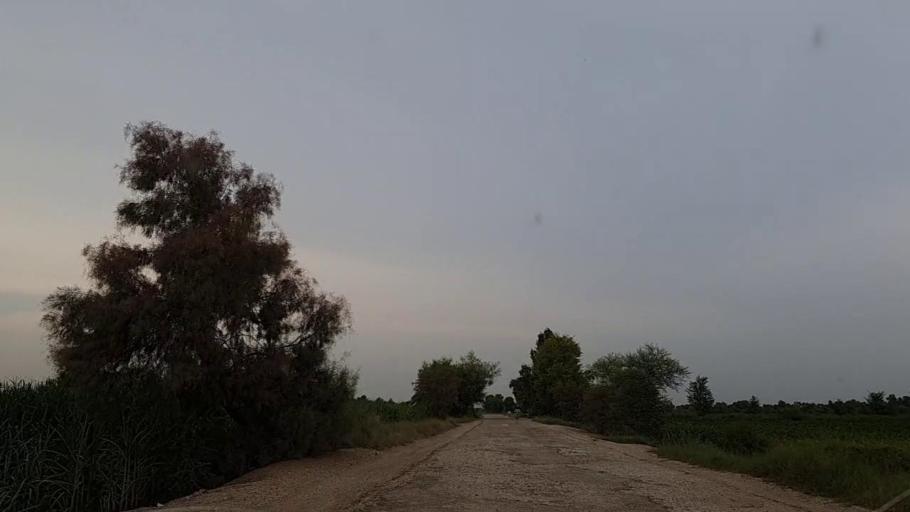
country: PK
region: Sindh
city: Mirpur Mathelo
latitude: 27.8862
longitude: 69.6393
